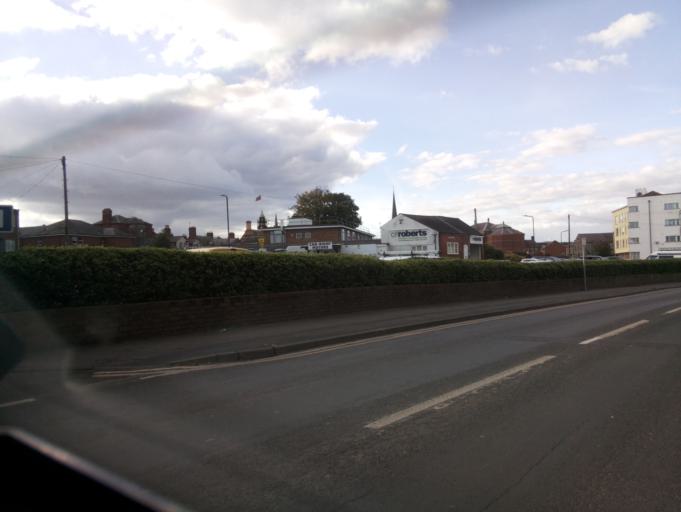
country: GB
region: England
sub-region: Herefordshire
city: Hereford
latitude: 52.0549
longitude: -2.7098
